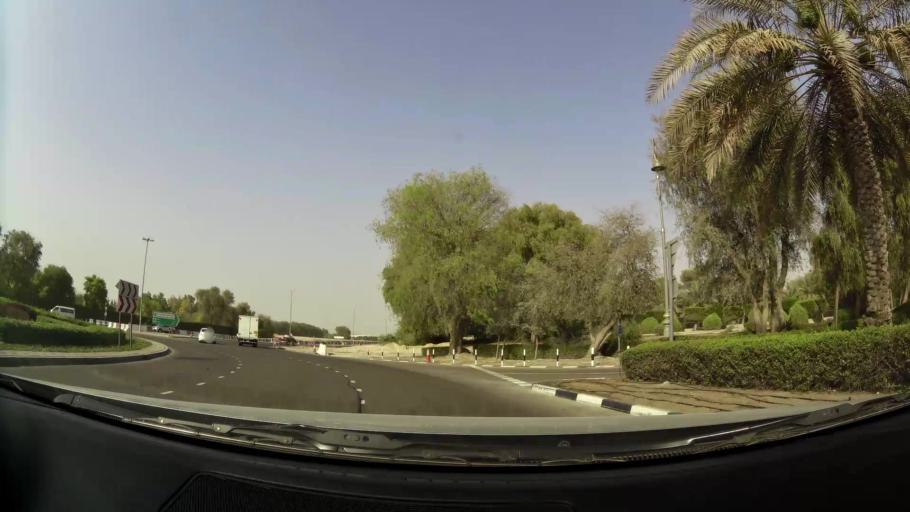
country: AE
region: Dubai
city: Dubai
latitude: 25.1476
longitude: 55.3311
